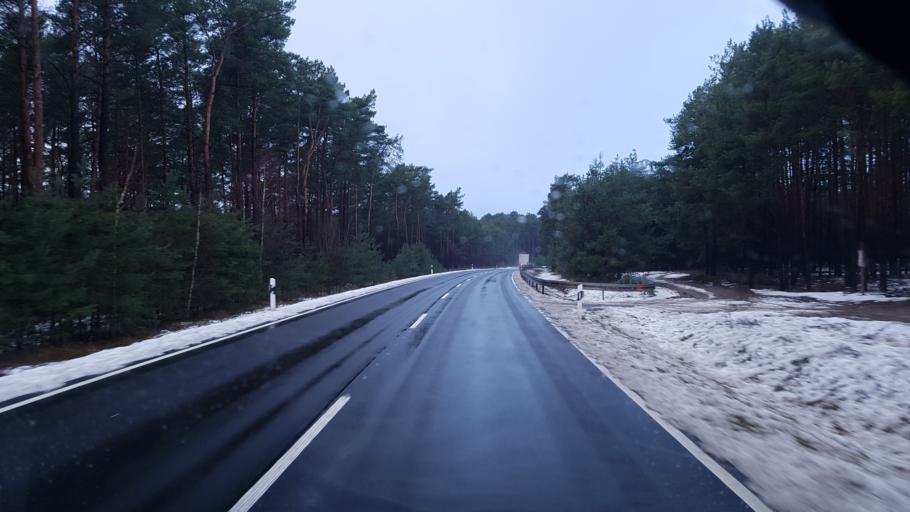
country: DE
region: Brandenburg
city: Schenkendobern
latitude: 51.8957
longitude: 14.6159
